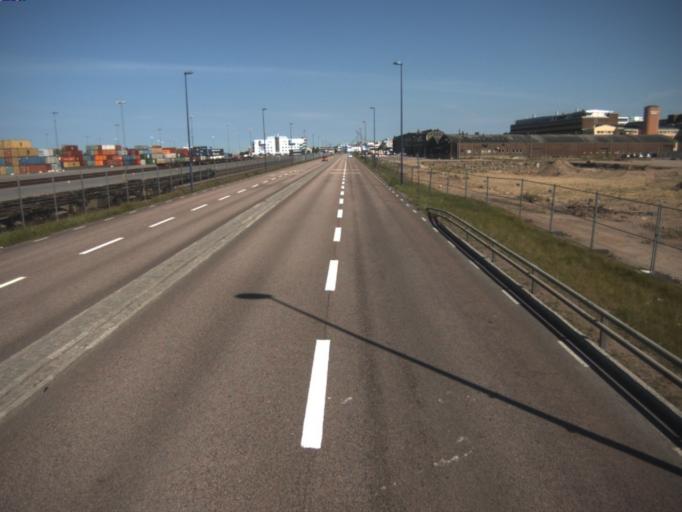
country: SE
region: Skane
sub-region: Helsingborg
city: Helsingborg
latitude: 56.0341
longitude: 12.6986
